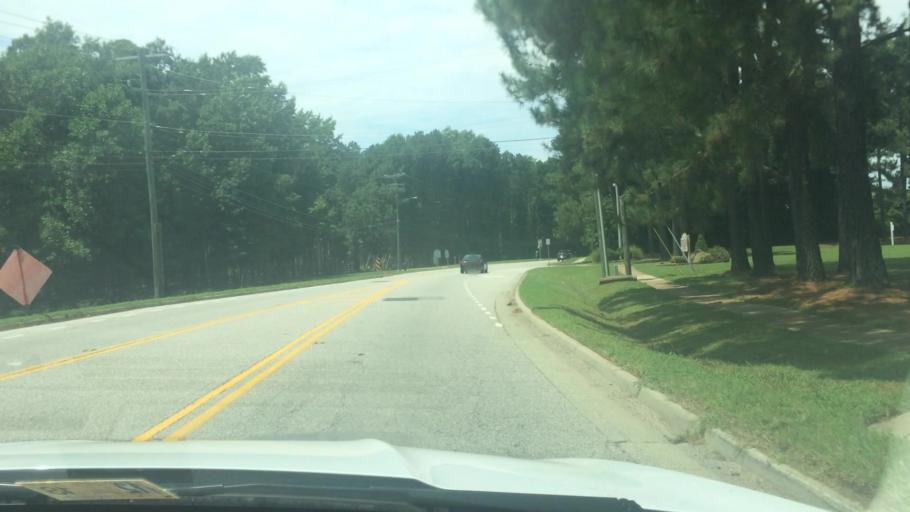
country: US
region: Virginia
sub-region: City of Williamsburg
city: Williamsburg
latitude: 37.2105
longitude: -76.6166
